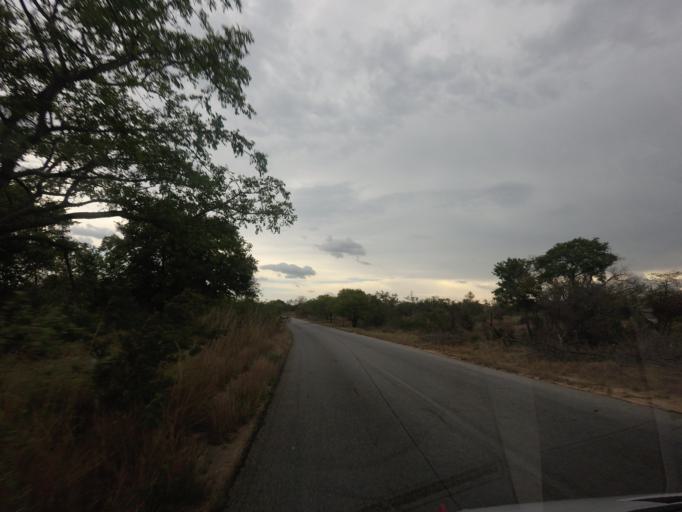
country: ZA
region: Limpopo
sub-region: Mopani District Municipality
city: Hoedspruit
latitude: -24.5264
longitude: 30.9659
